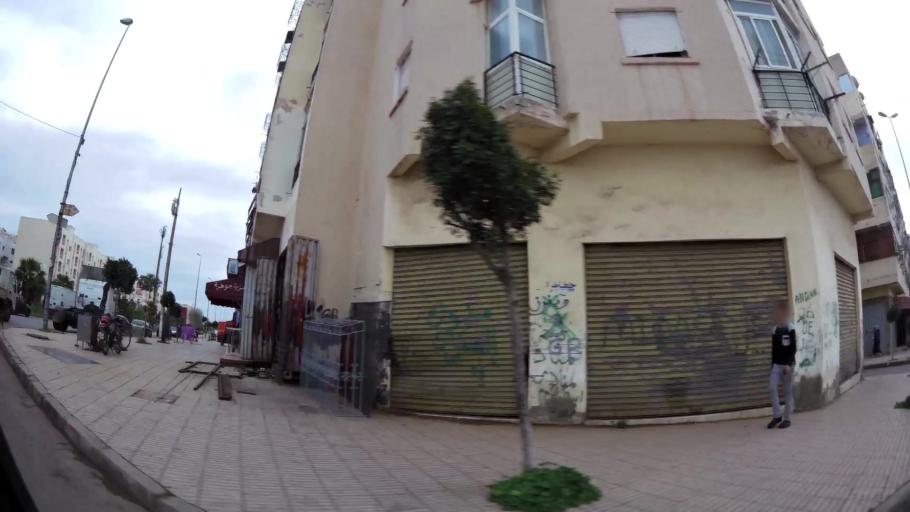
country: MA
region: Grand Casablanca
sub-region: Mediouna
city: Tit Mellil
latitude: 33.5581
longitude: -7.5331
